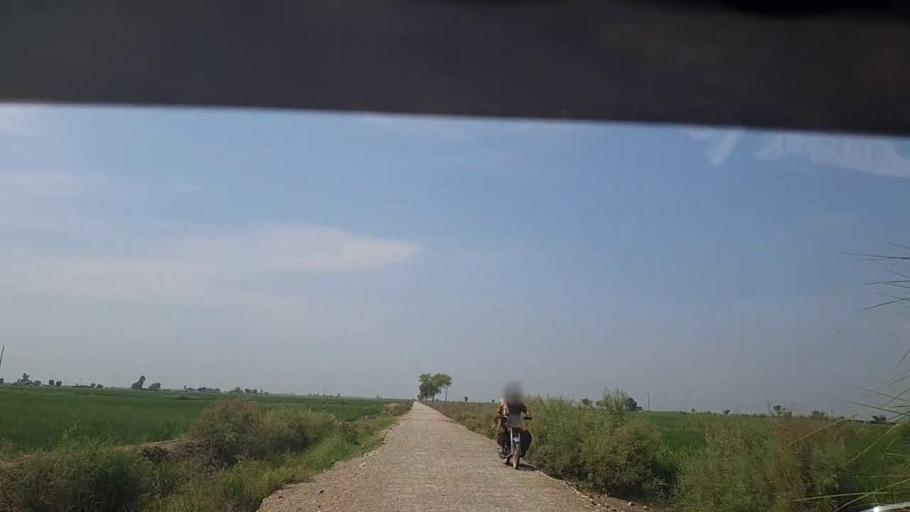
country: PK
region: Sindh
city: Thul
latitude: 28.2137
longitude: 68.6835
